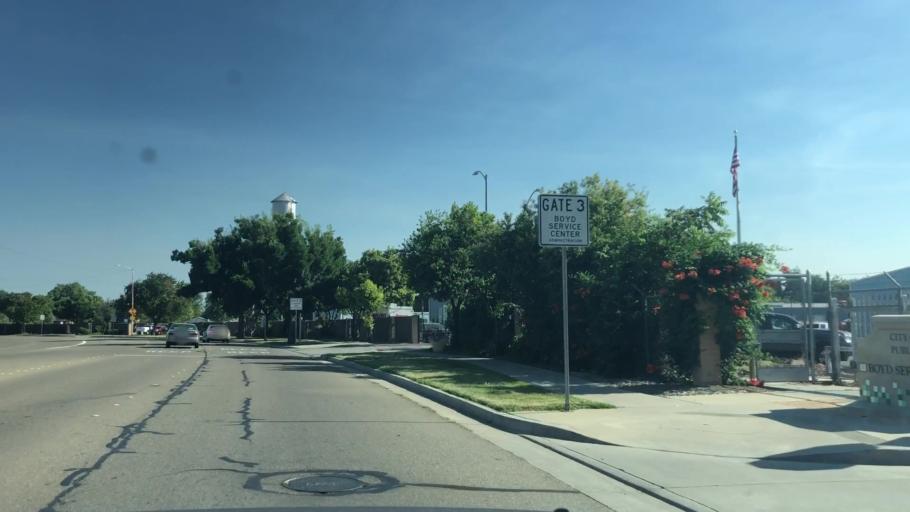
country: US
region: California
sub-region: San Joaquin County
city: Tracy
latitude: 37.7349
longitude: -121.4348
